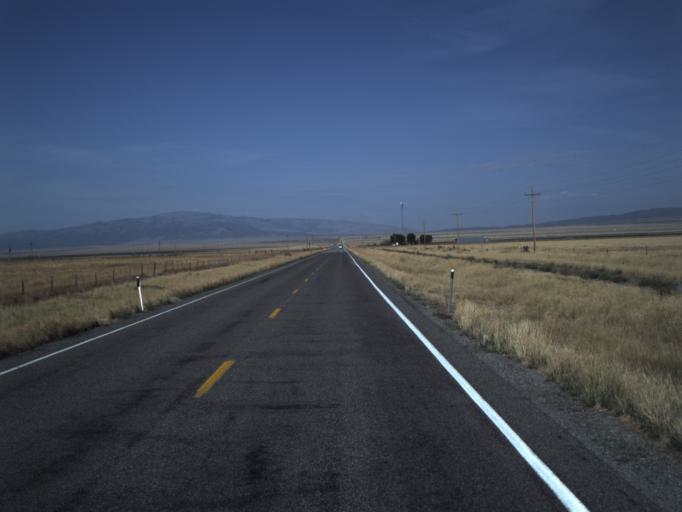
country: US
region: Idaho
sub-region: Oneida County
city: Malad City
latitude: 41.9665
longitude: -112.9159
